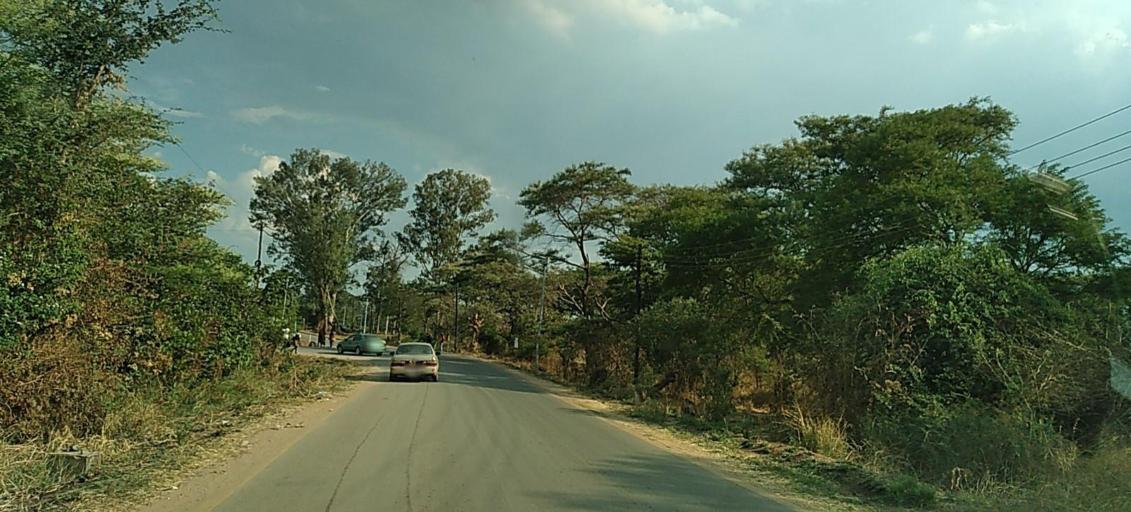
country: ZM
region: Lusaka
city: Lusaka
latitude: -15.5454
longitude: 28.2470
